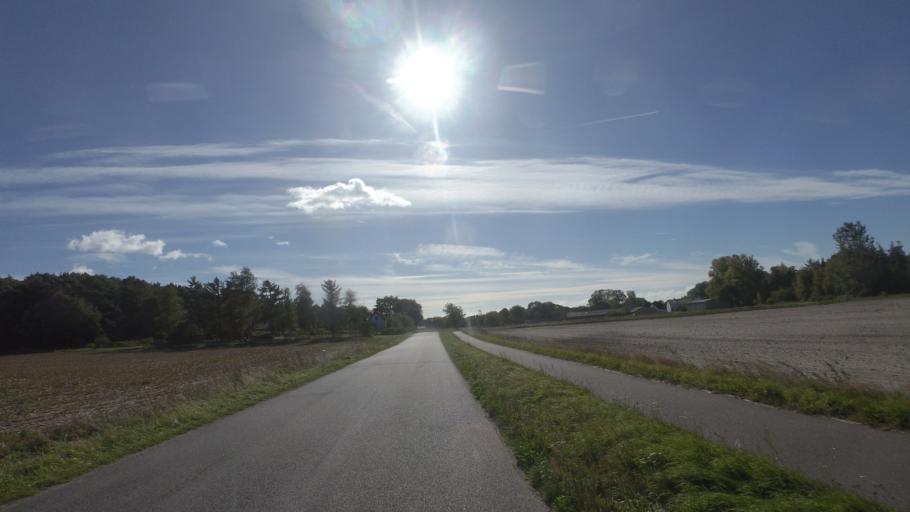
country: DK
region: Capital Region
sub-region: Bornholm Kommune
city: Akirkeby
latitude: 55.0110
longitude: 14.9916
